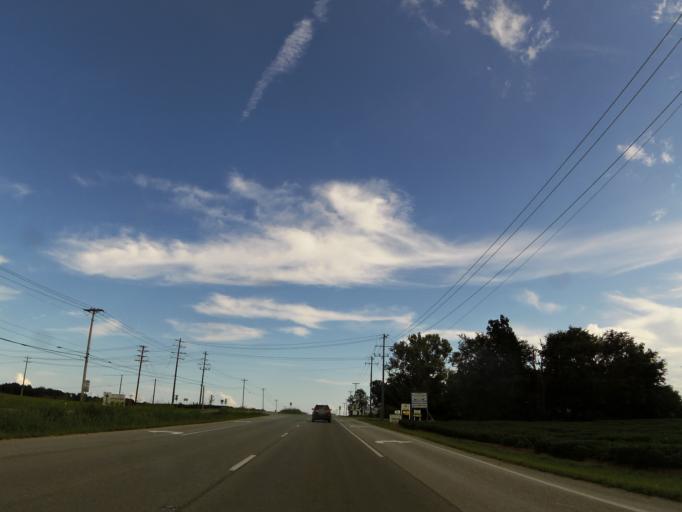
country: US
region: Kentucky
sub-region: Christian County
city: Oak Grove
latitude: 36.7224
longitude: -87.4608
